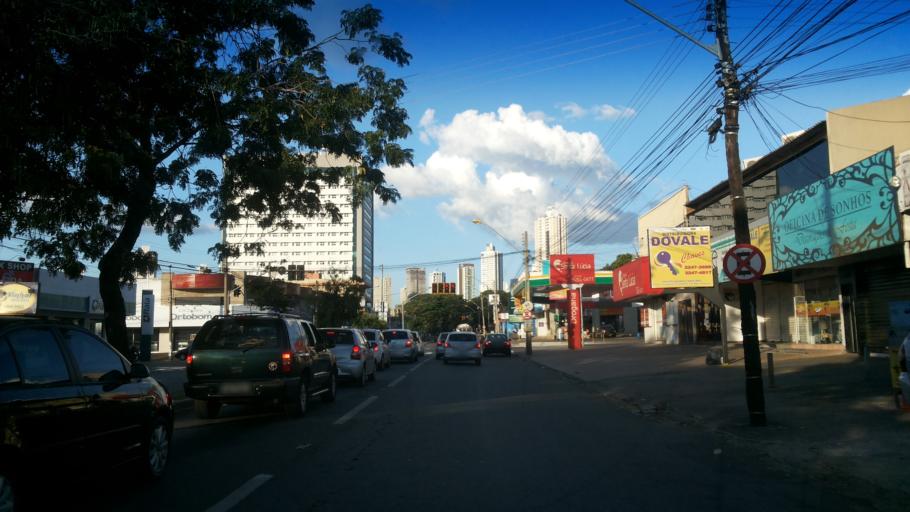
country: BR
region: Goias
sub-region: Goiania
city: Goiania
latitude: -16.7083
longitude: -49.2847
